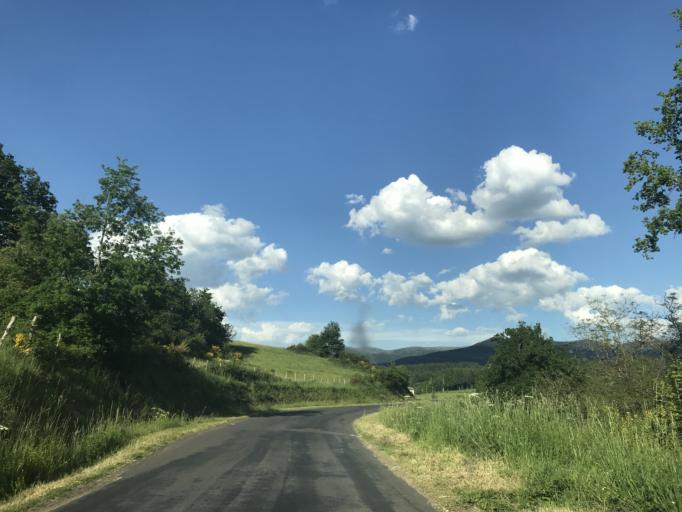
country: FR
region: Auvergne
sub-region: Departement du Puy-de-Dome
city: Job
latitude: 45.6544
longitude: 3.6693
